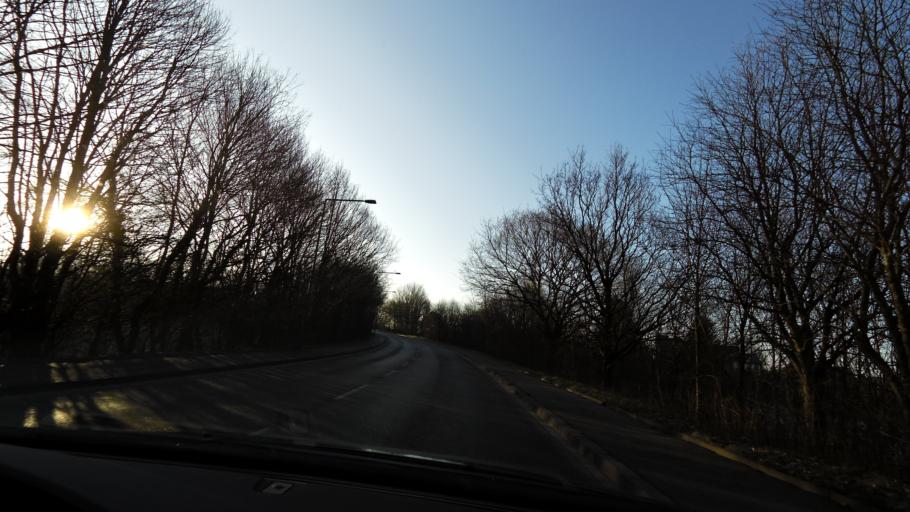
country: NL
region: Limburg
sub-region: Gemeente Vaals
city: Vaals
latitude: 50.8024
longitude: 6.0476
